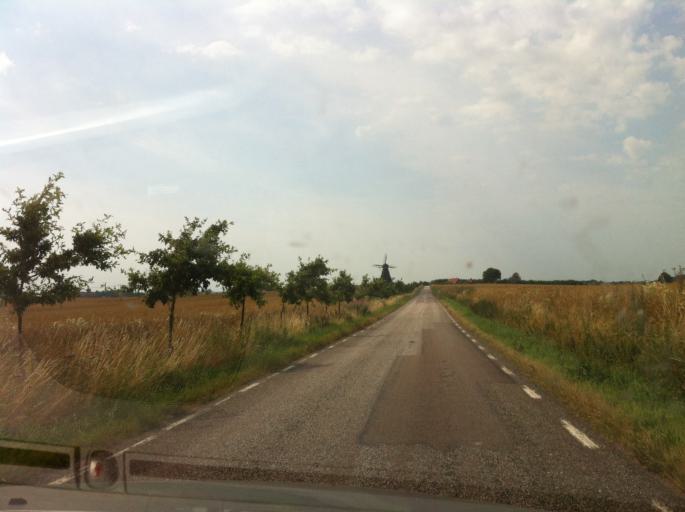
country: SE
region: Skane
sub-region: Svalovs Kommun
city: Svaloev
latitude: 55.9135
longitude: 13.1703
